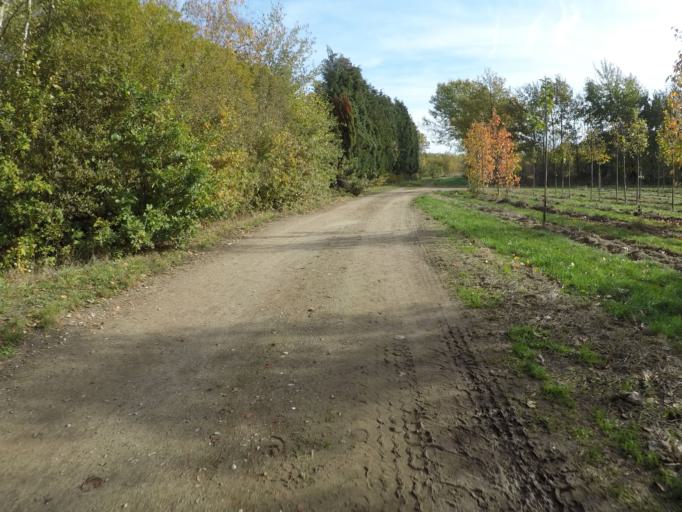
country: BE
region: Flanders
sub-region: Provincie Vlaams-Brabant
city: Begijnendijk
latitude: 51.0045
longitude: 4.7970
